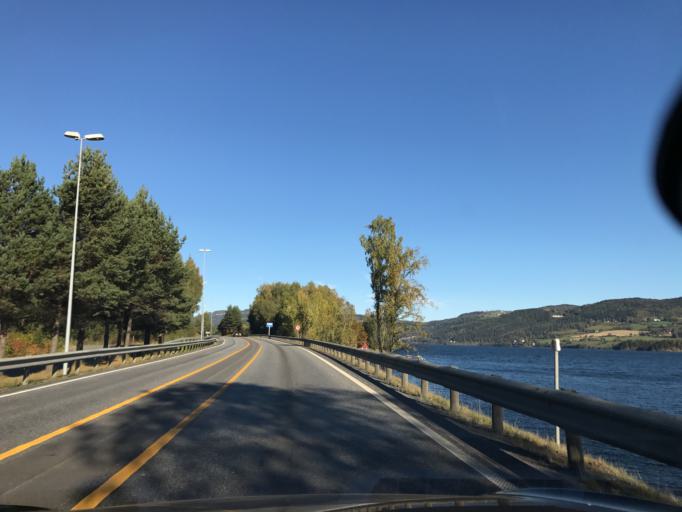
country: NO
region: Hedmark
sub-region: Ringsaker
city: Moelv
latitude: 60.9310
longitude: 10.6545
